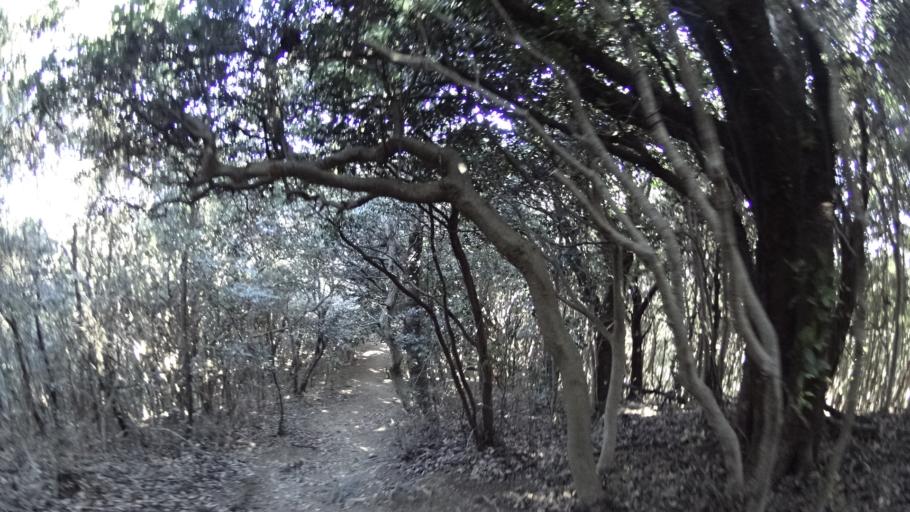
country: JP
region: Shizuoka
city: Kosai-shi
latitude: 34.7518
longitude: 137.4751
